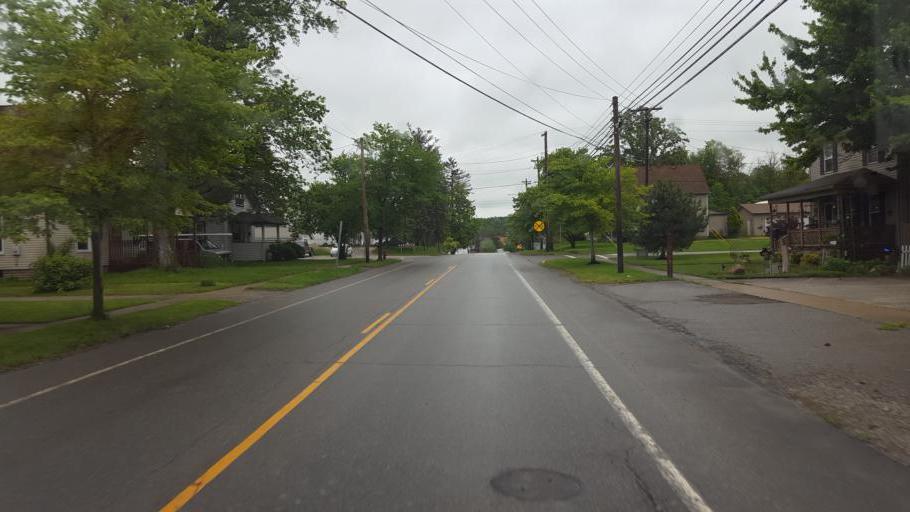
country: US
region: Ohio
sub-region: Medina County
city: Lodi
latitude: 41.0323
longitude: -82.0188
